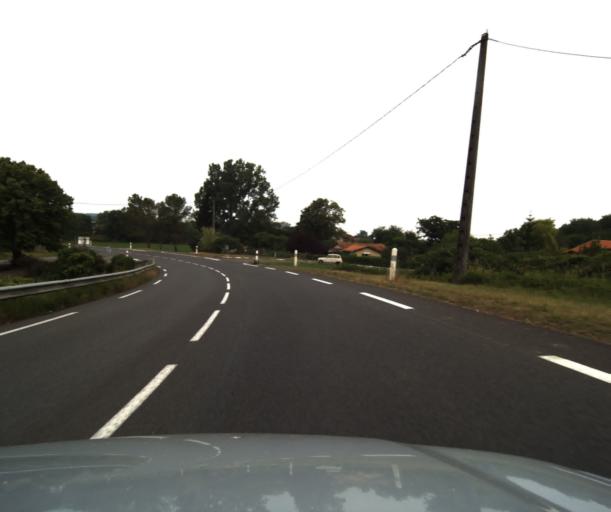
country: FR
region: Midi-Pyrenees
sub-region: Departement du Gers
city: Mielan
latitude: 43.4261
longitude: 0.2947
